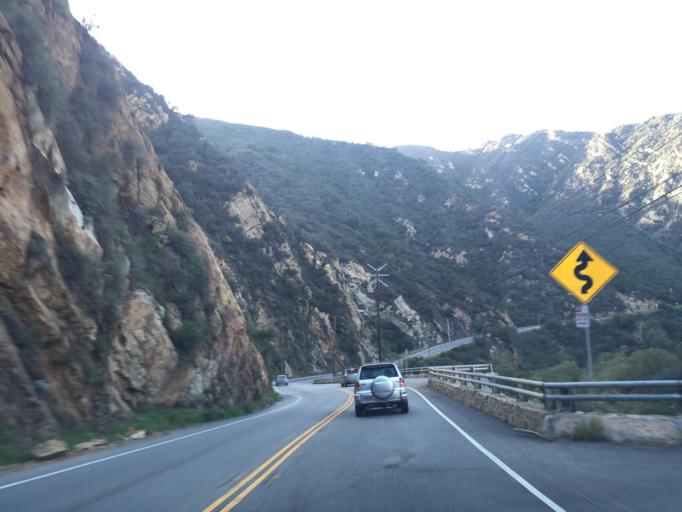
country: US
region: California
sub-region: Los Angeles County
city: Malibu Beach
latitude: 34.0633
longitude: -118.7058
